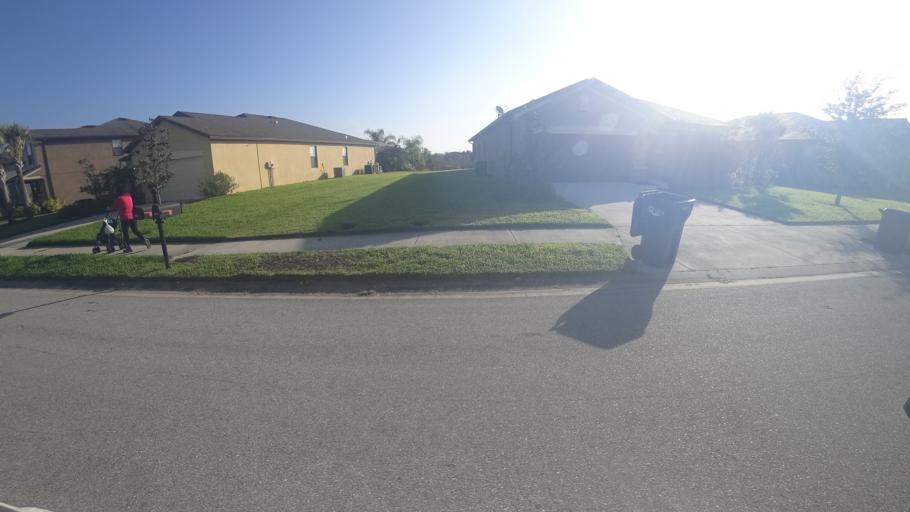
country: US
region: Florida
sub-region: Manatee County
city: Ellenton
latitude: 27.5651
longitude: -82.4549
